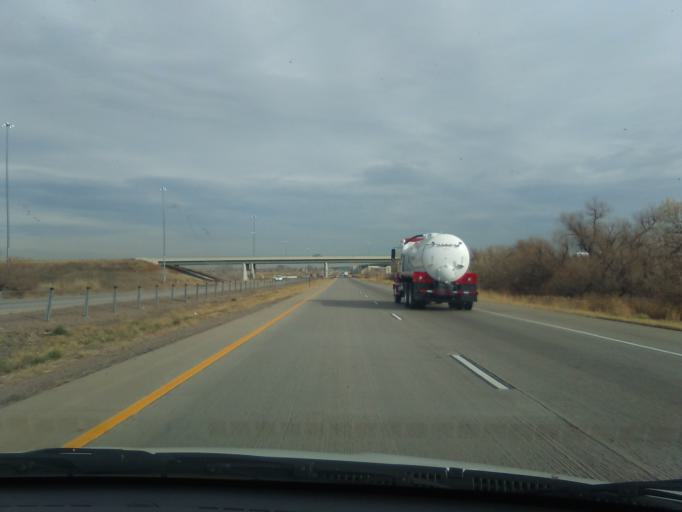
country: US
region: Colorado
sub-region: Adams County
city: Brighton
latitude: 39.9225
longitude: -104.8063
